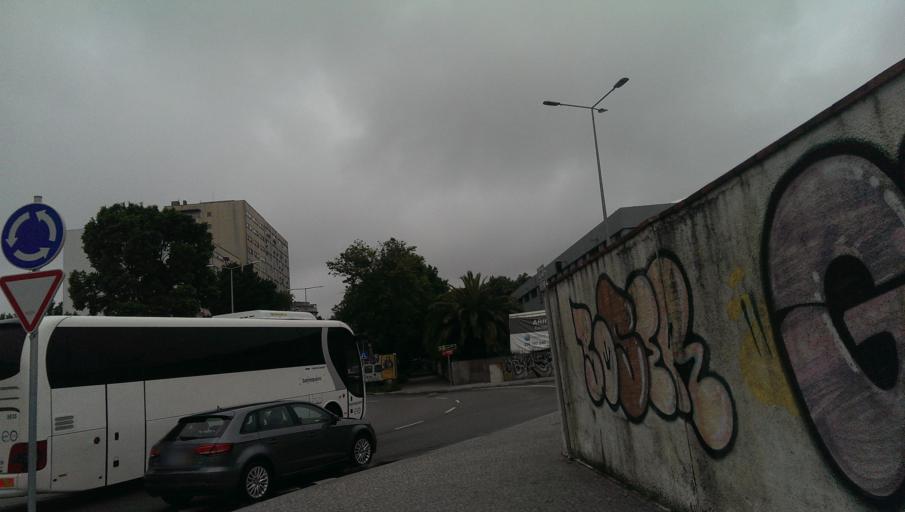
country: PT
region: Porto
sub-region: Matosinhos
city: Matosinhos
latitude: 41.1768
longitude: -8.6810
